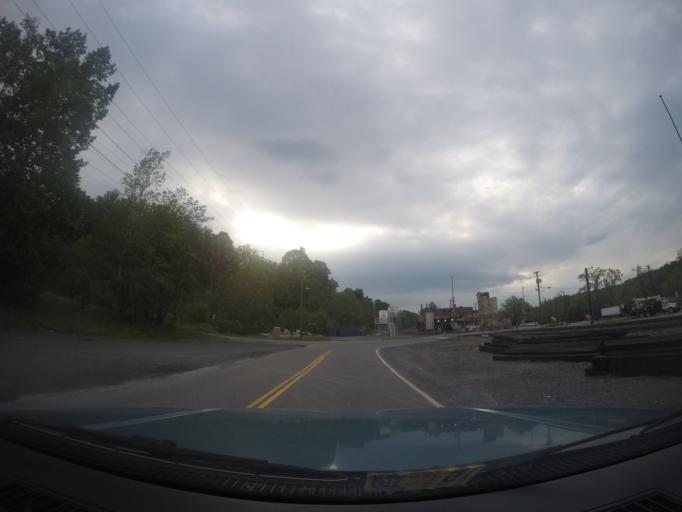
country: US
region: Virginia
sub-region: City of Lynchburg
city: Lynchburg
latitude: 37.3984
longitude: -79.1226
